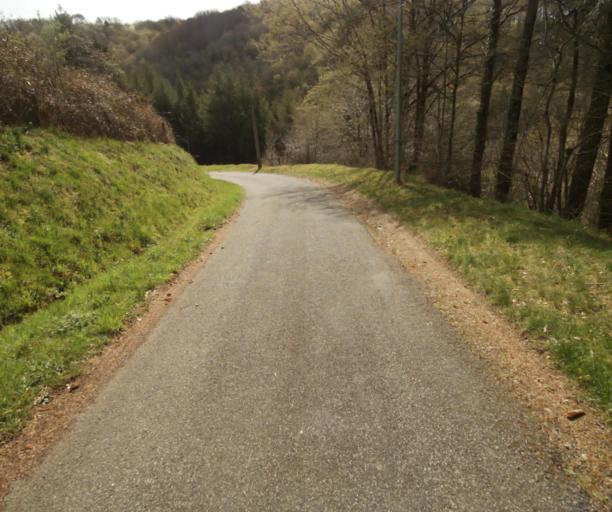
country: FR
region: Limousin
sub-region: Departement de la Correze
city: Laguenne
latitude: 45.2495
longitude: 1.8207
